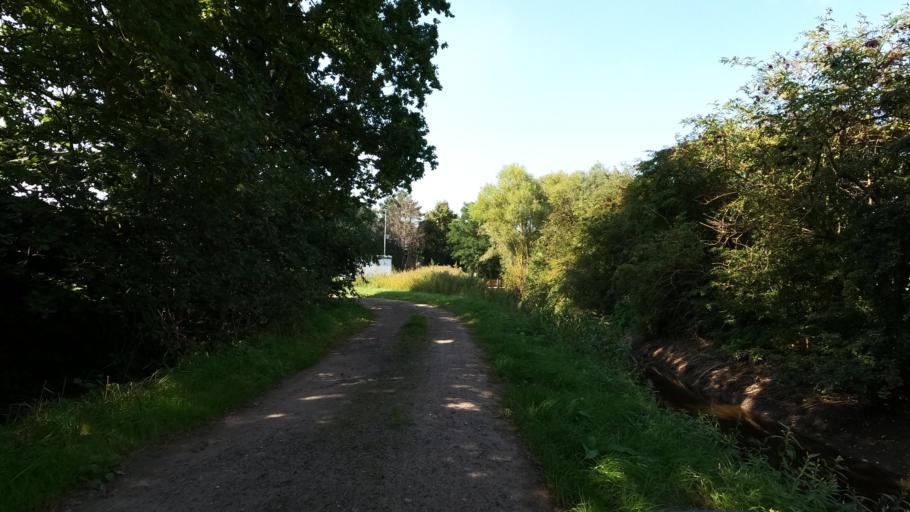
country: BE
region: Flanders
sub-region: Provincie Vlaams-Brabant
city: Boortmeerbeek
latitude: 50.9905
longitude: 4.5820
